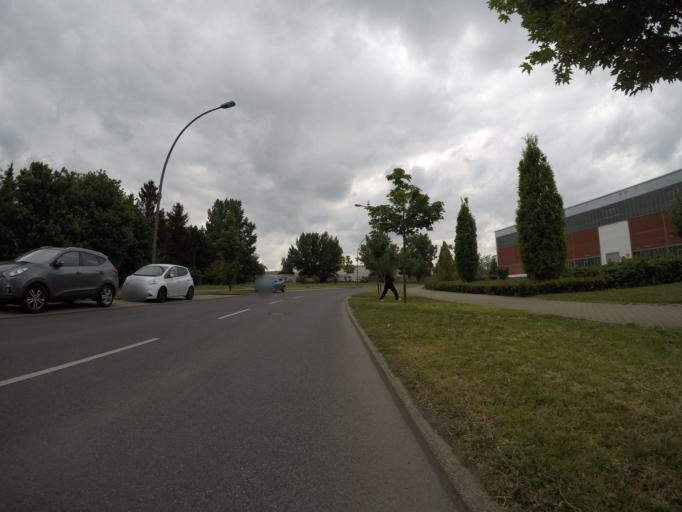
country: DE
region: Berlin
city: Falkenberg
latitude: 52.5448
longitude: 13.5369
